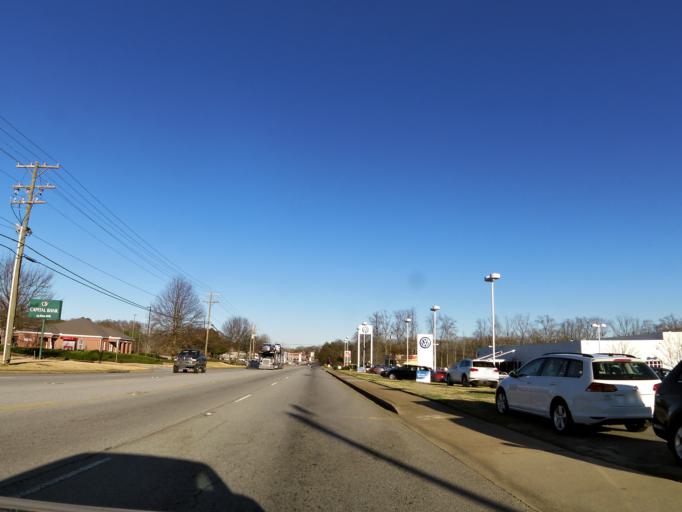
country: US
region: South Carolina
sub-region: Spartanburg County
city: Fairforest
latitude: 34.9175
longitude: -82.0020
